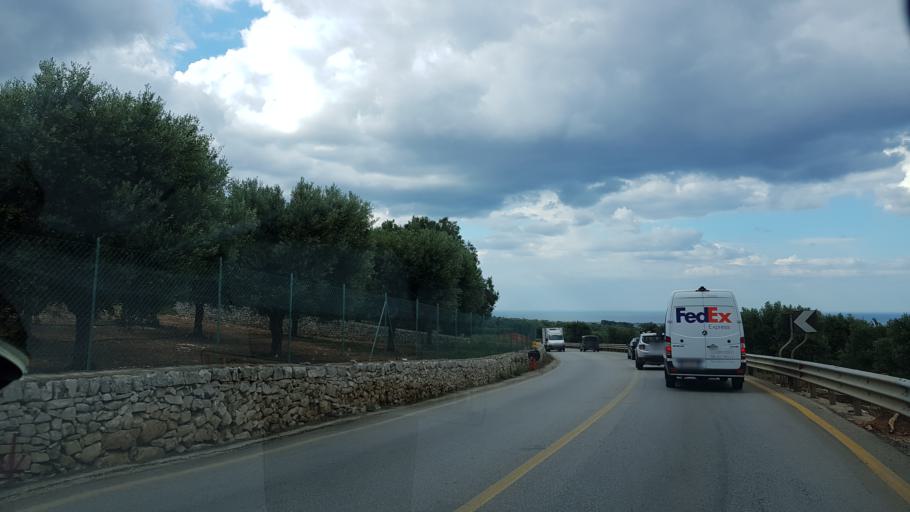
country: IT
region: Apulia
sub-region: Provincia di Brindisi
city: Lamie di Olimpie-Selva
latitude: 40.8177
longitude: 17.3456
